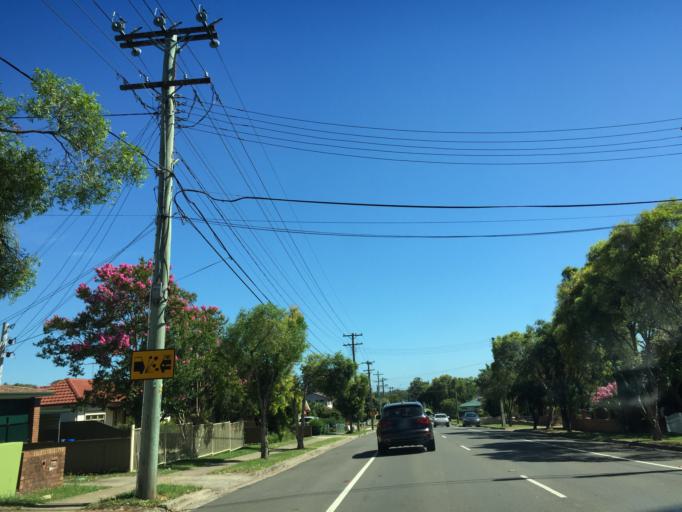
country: AU
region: New South Wales
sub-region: Blacktown
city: Blacktown
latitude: -33.7743
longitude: 150.8956
